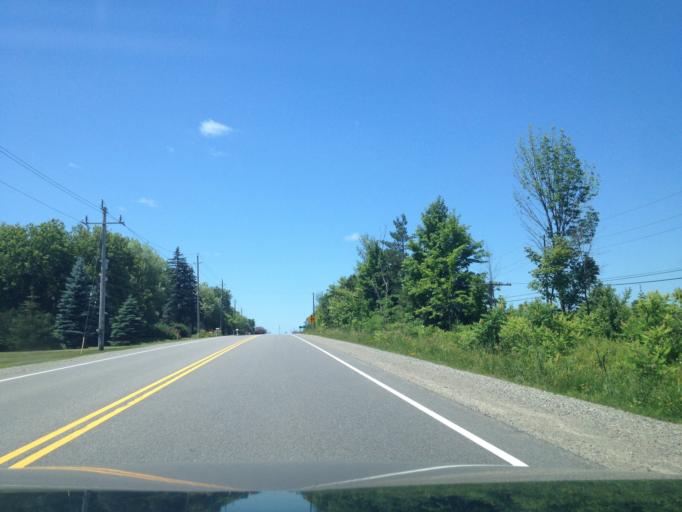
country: CA
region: Ontario
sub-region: Halton
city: Milton
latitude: 43.6317
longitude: -80.0598
